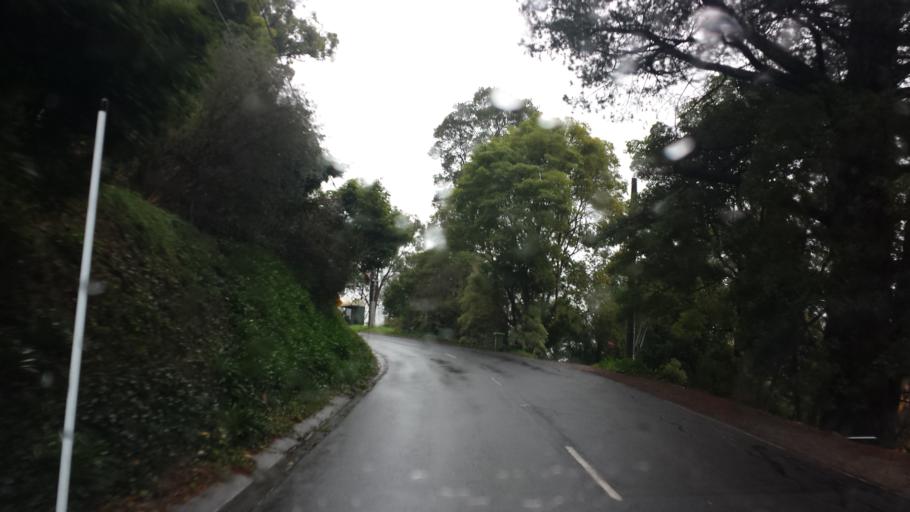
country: AU
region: Victoria
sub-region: Yarra Ranges
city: Monbulk
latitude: -37.8868
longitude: 145.3863
